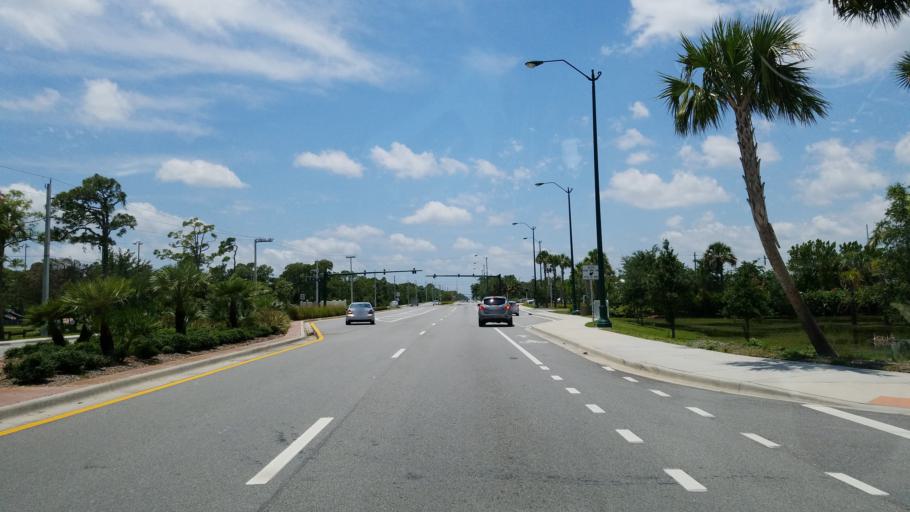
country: US
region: Florida
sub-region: Martin County
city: Palm City
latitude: 27.1612
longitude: -80.2678
